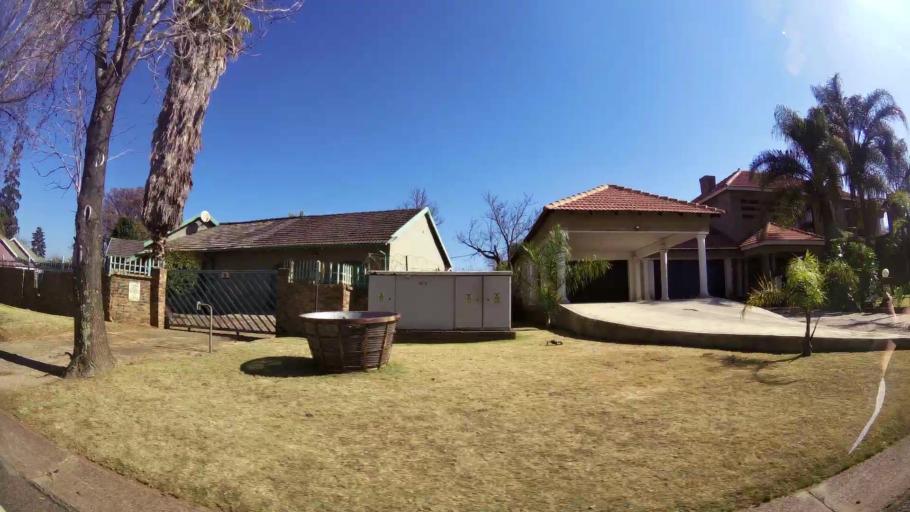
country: ZA
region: Mpumalanga
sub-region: Nkangala District Municipality
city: Witbank
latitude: -25.8298
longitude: 29.2438
